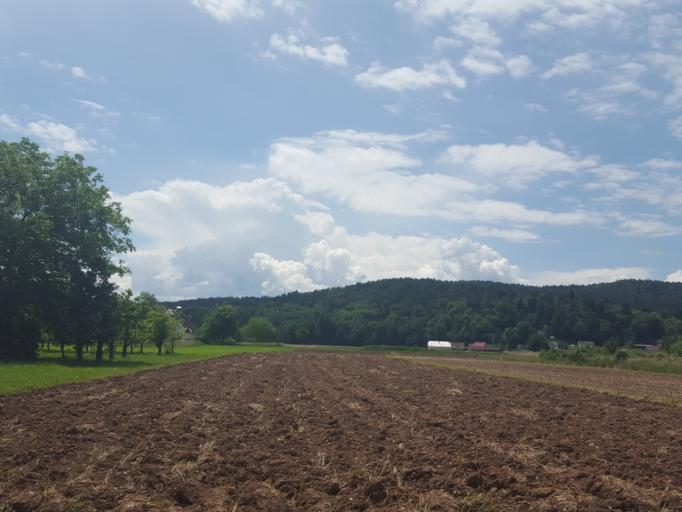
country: SI
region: Skofljica
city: Lavrica
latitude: 46.0451
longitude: 14.5629
